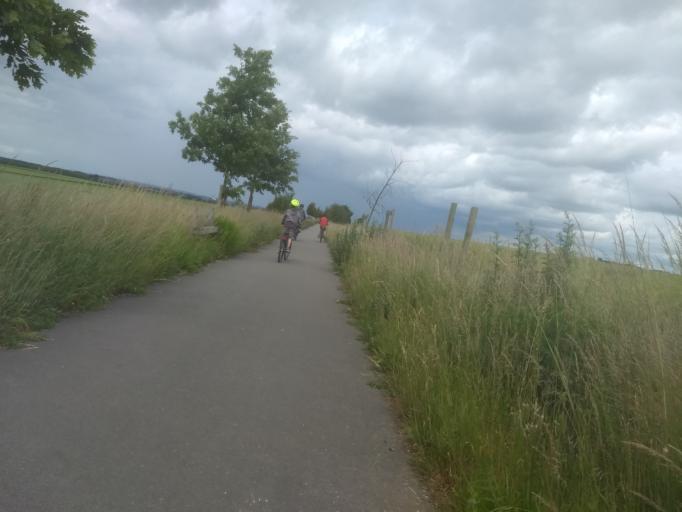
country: FR
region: Nord-Pas-de-Calais
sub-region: Departement du Pas-de-Calais
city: Riviere
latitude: 50.2549
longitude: 2.7003
